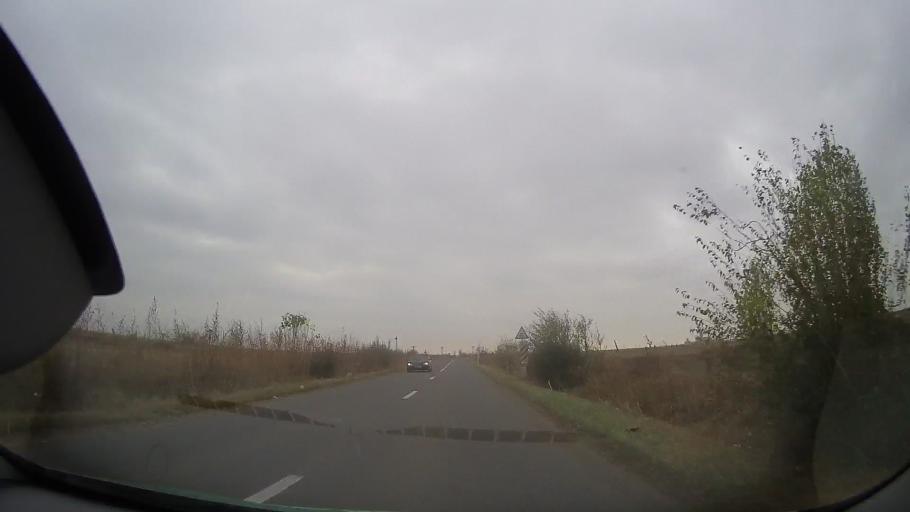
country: RO
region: Ialomita
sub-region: Comuna Manasia
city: Manasia
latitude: 44.7250
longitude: 26.6914
